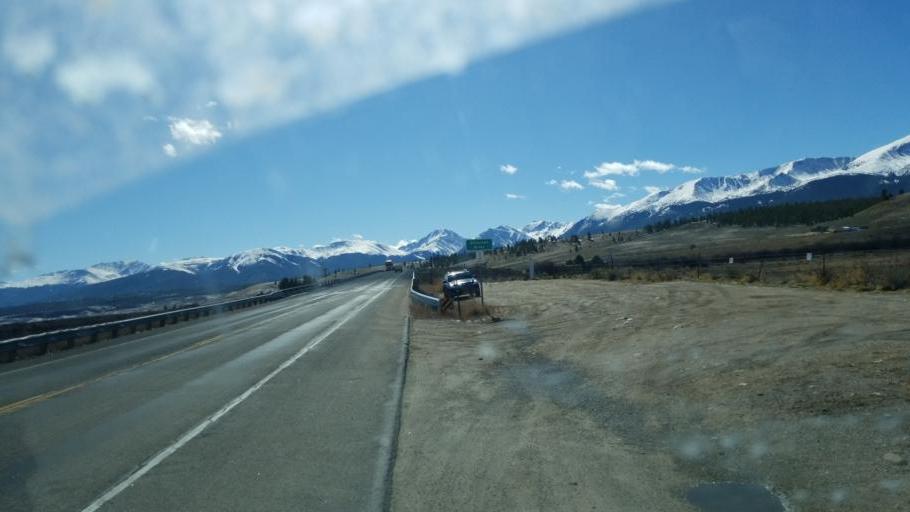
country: US
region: Colorado
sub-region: Lake County
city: Leadville
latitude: 39.1693
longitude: -106.3236
